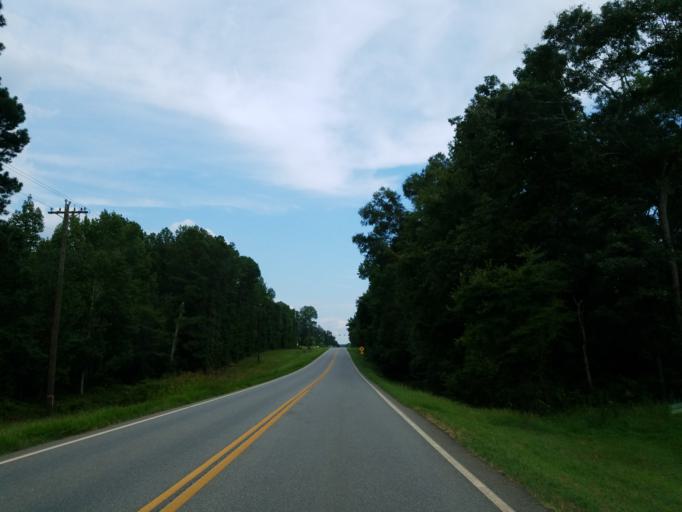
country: US
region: Georgia
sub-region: Dooly County
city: Unadilla
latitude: 32.3233
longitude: -83.7188
